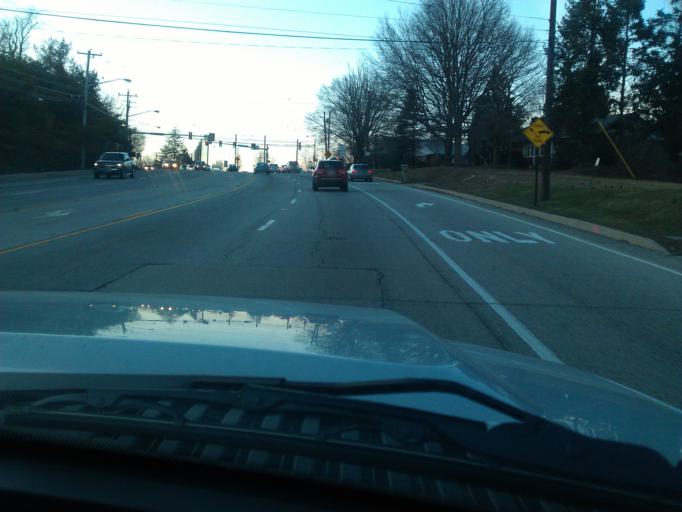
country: US
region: Pennsylvania
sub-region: Montgomery County
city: Plymouth Meeting
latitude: 40.1208
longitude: -75.2876
